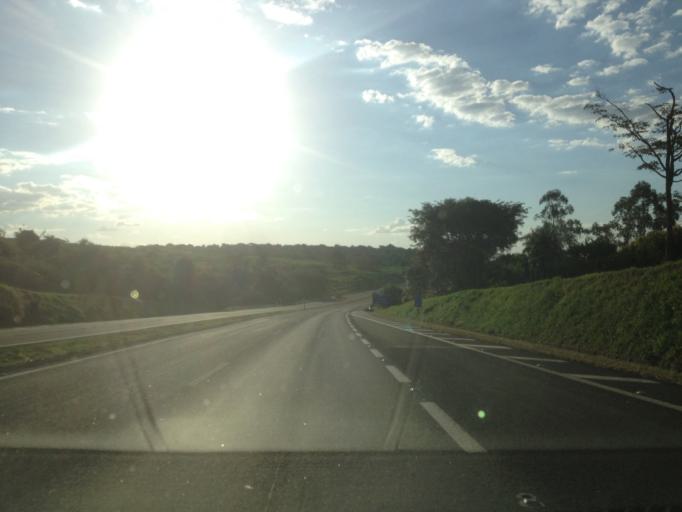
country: BR
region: Sao Paulo
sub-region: Brotas
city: Brotas
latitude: -22.2610
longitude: -48.2382
